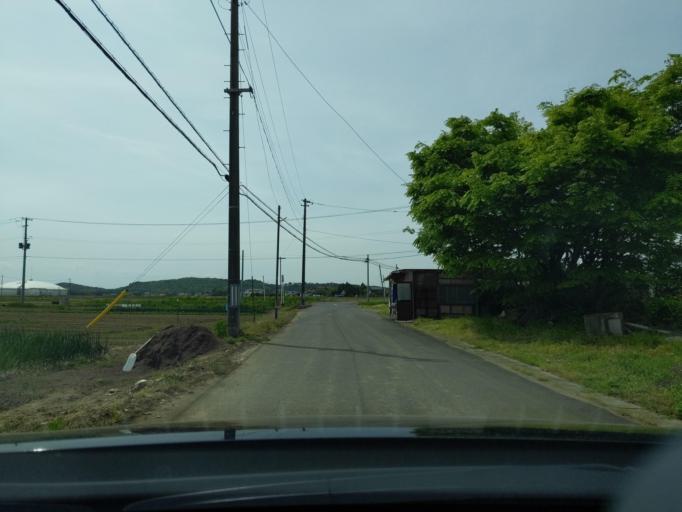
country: JP
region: Fukushima
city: Koriyama
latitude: 37.4041
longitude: 140.2727
